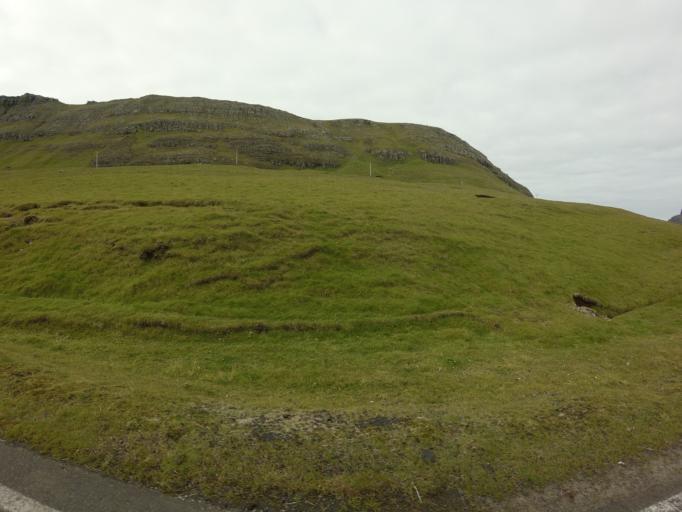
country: FO
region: Suduroy
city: Tvoroyri
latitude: 61.5918
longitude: -6.9472
